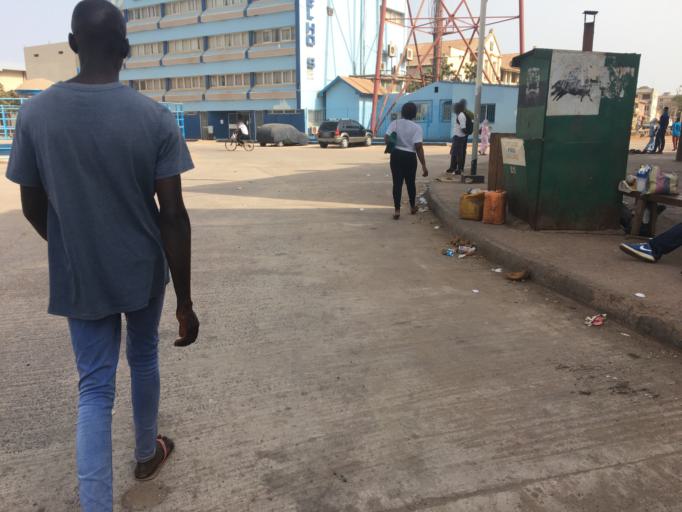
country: GM
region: Banjul
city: Banjul
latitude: 13.4527
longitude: -16.5756
